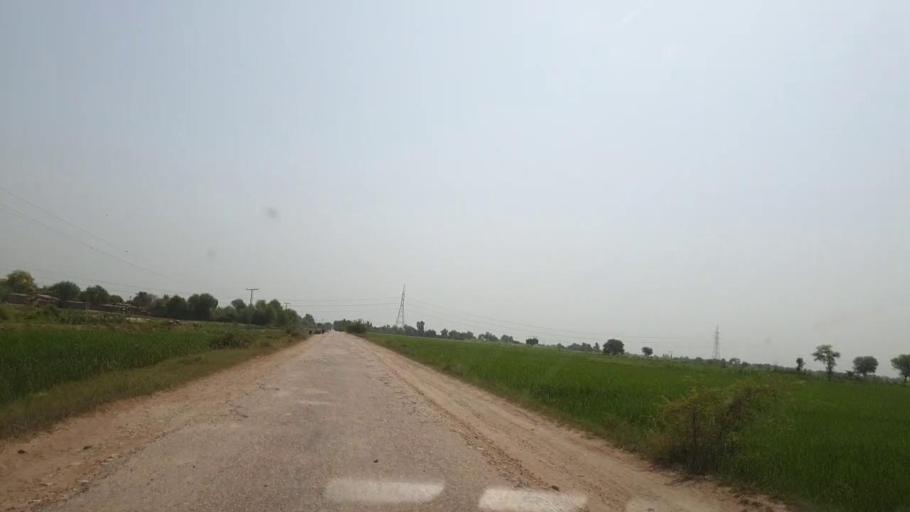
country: PK
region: Sindh
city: Lakhi
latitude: 27.8796
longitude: 68.6721
